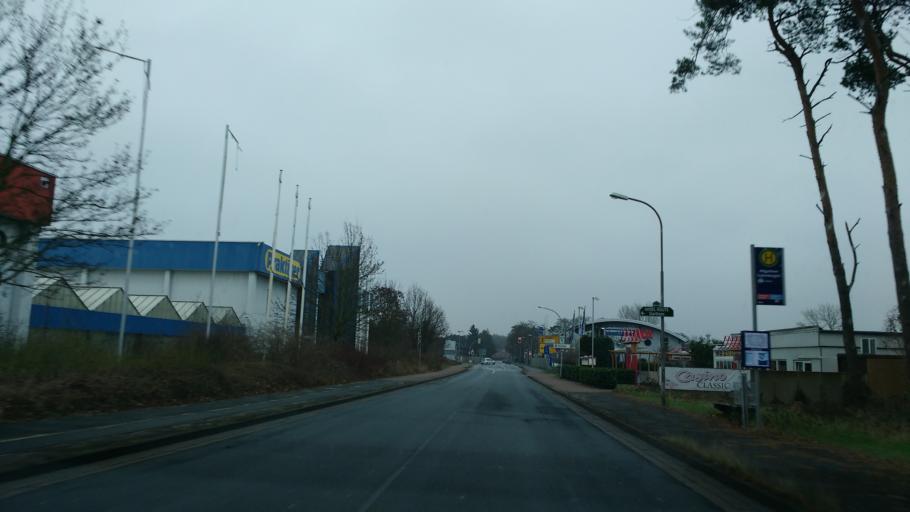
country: DE
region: Lower Saxony
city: Garbsen
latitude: 52.4194
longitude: 9.5724
